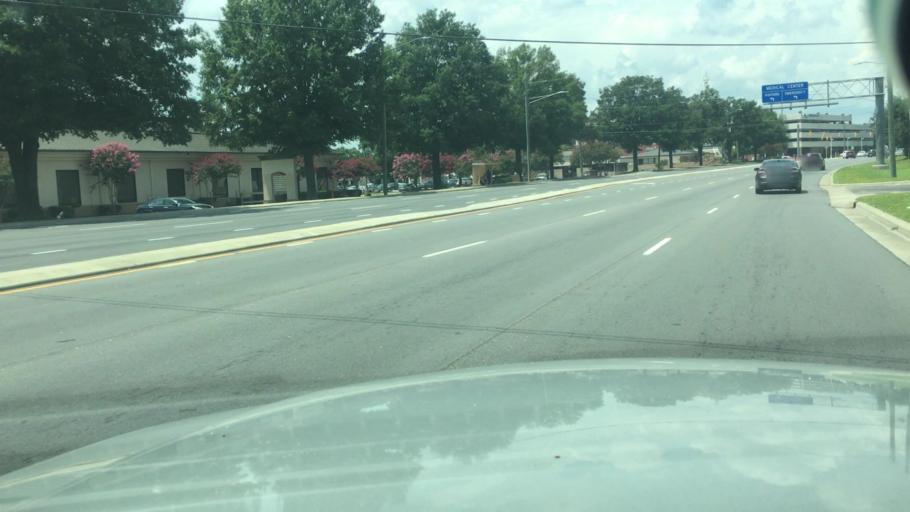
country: US
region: North Carolina
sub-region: Cumberland County
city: Fayetteville
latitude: 35.0286
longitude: -78.9285
